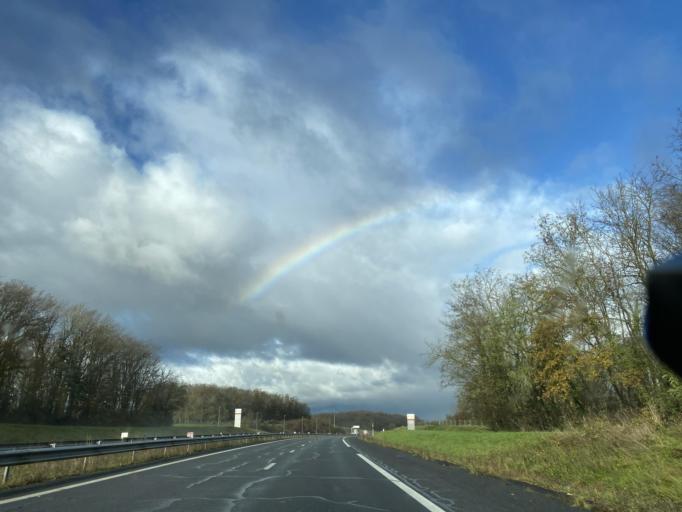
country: FR
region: Centre
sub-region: Departement du Cher
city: Orval
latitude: 46.7541
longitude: 2.4144
